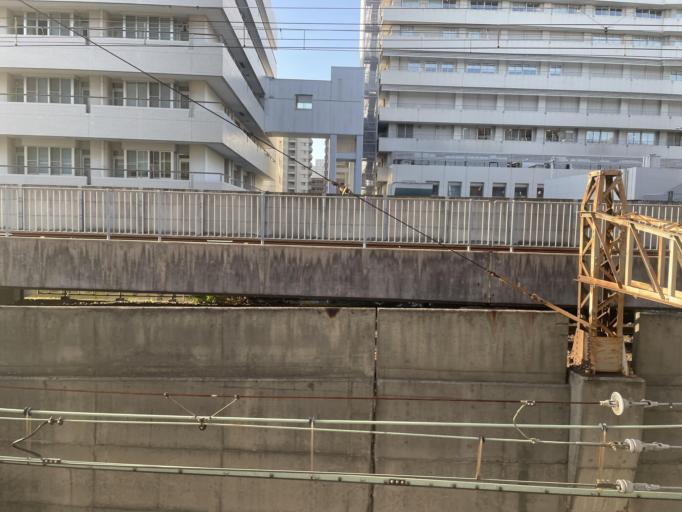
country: JP
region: Osaka
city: Osaka-shi
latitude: 34.6654
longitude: 135.5261
